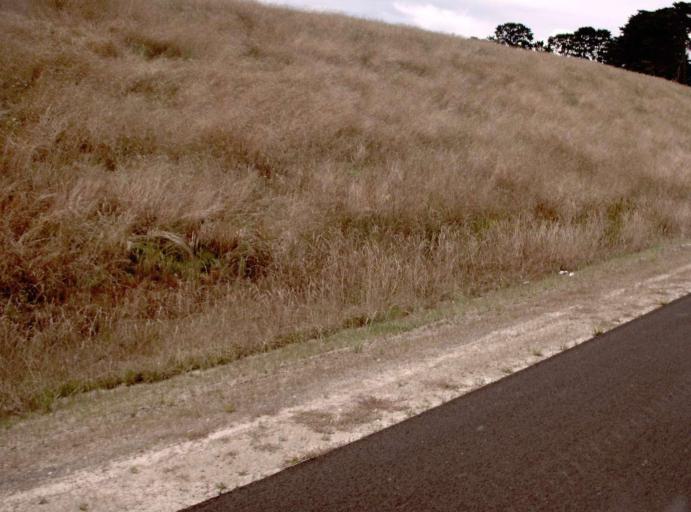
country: AU
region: Victoria
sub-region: Mornington Peninsula
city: Moorooduc
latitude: -38.2642
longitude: 145.1049
